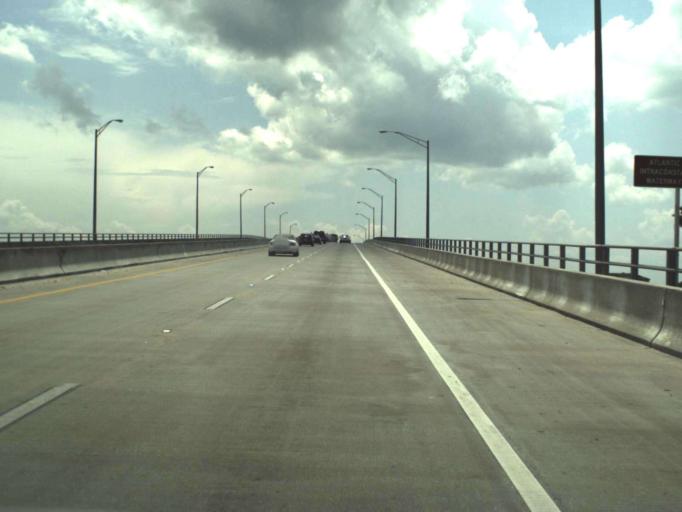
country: US
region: Florida
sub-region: Volusia County
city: New Smyrna Beach
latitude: 29.0250
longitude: -80.9144
